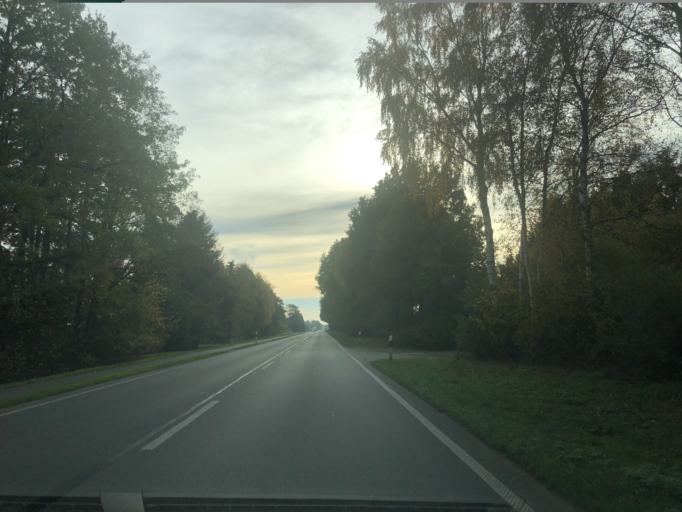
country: DE
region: Lower Saxony
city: Edewecht
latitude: 53.0746
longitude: 7.9283
